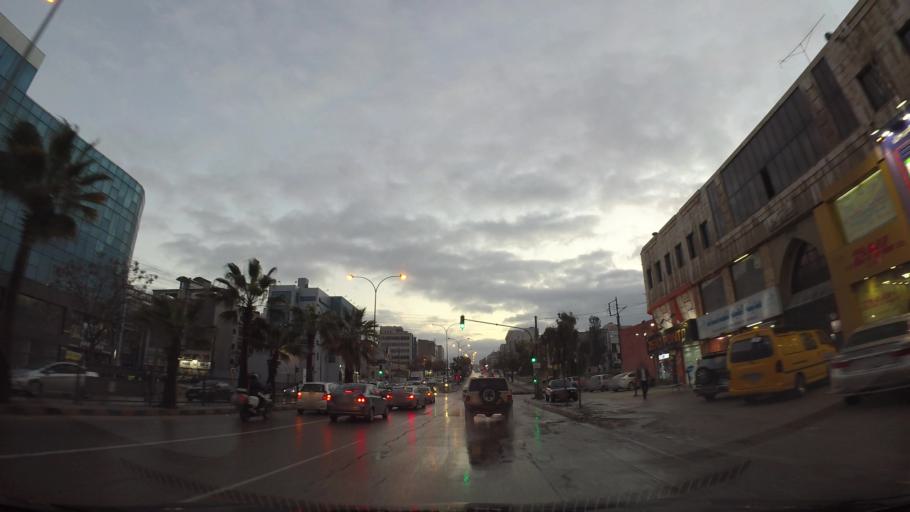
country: JO
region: Amman
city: Al Jubayhah
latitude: 31.9815
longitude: 35.8927
